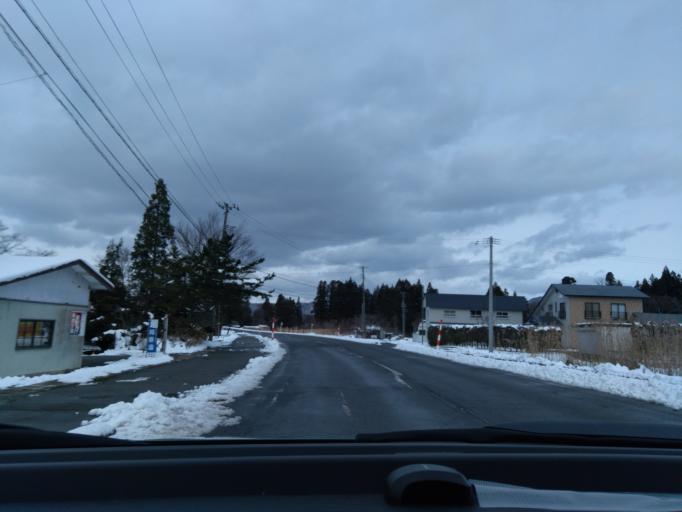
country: JP
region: Akita
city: Kakunodatemachi
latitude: 39.6198
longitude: 140.6314
